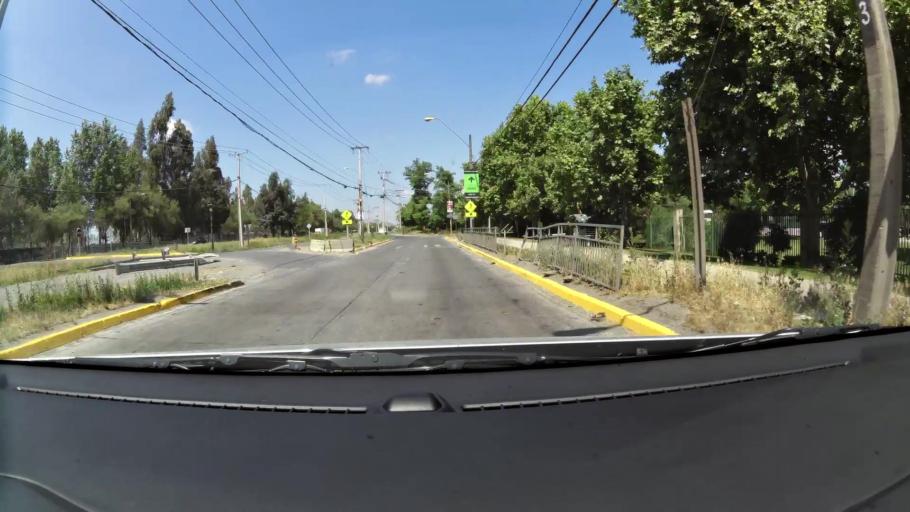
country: CL
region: Santiago Metropolitan
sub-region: Provincia de Maipo
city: San Bernardo
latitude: -33.5311
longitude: -70.7323
